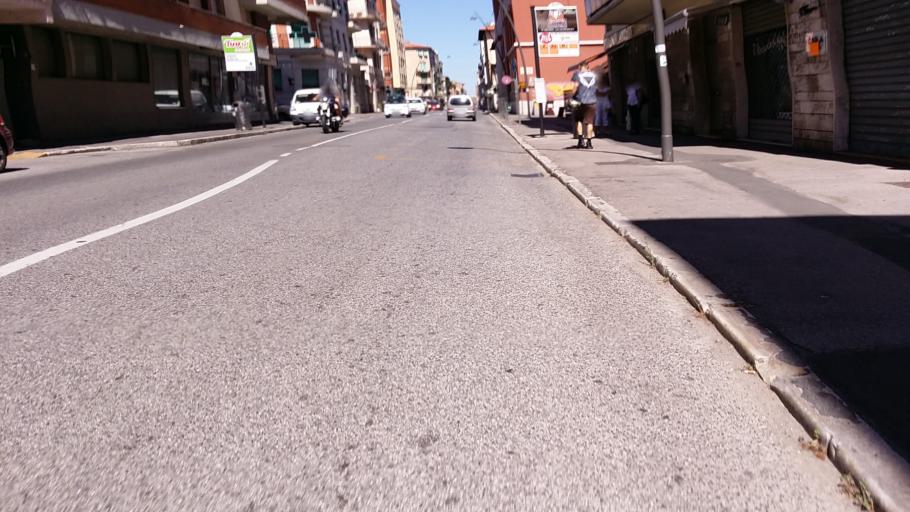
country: IT
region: Tuscany
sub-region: Provincia di Livorno
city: Livorno
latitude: 43.5380
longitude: 10.3178
